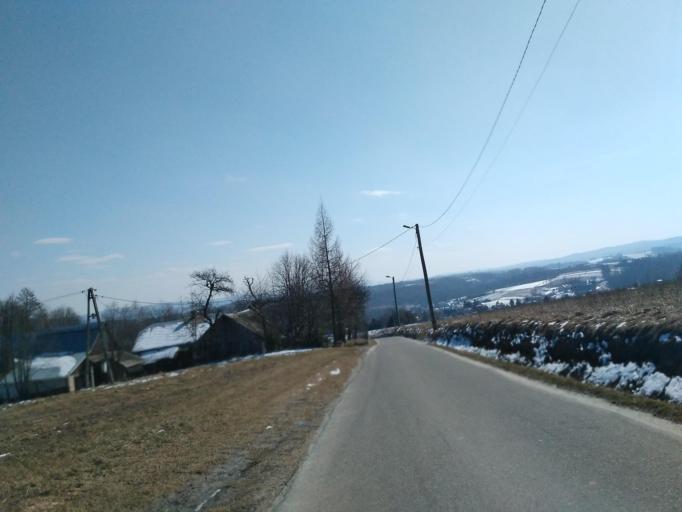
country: PL
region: Subcarpathian Voivodeship
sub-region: Powiat brzozowski
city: Jasienica Rosielna
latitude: 49.7581
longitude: 21.9346
